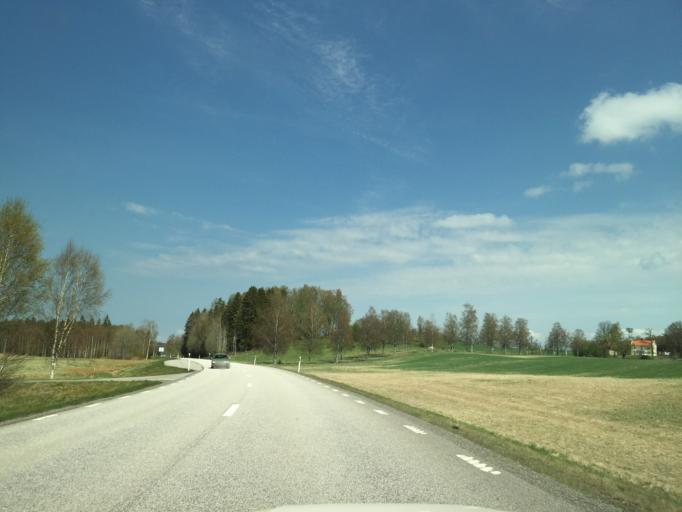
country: SE
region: Vaestra Goetaland
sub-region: Bengtsfors Kommun
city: Dals Langed
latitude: 58.8625
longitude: 12.1874
